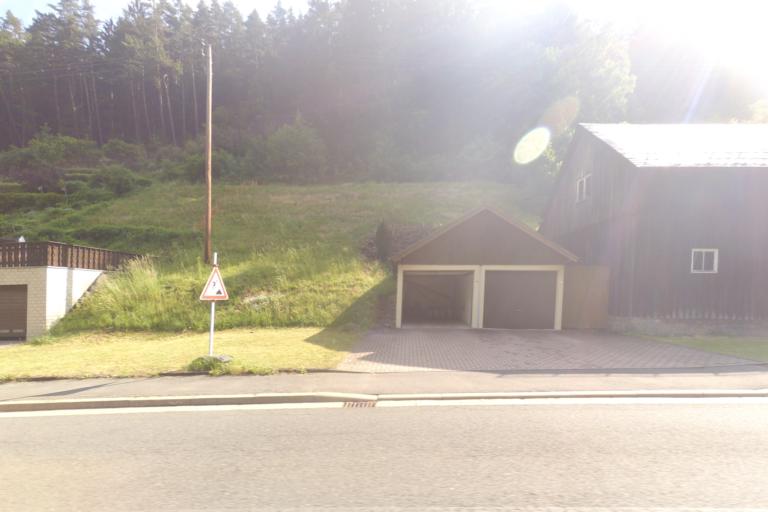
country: DE
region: Bavaria
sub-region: Upper Franconia
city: Ludwigsstadt
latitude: 50.4976
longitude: 11.3727
